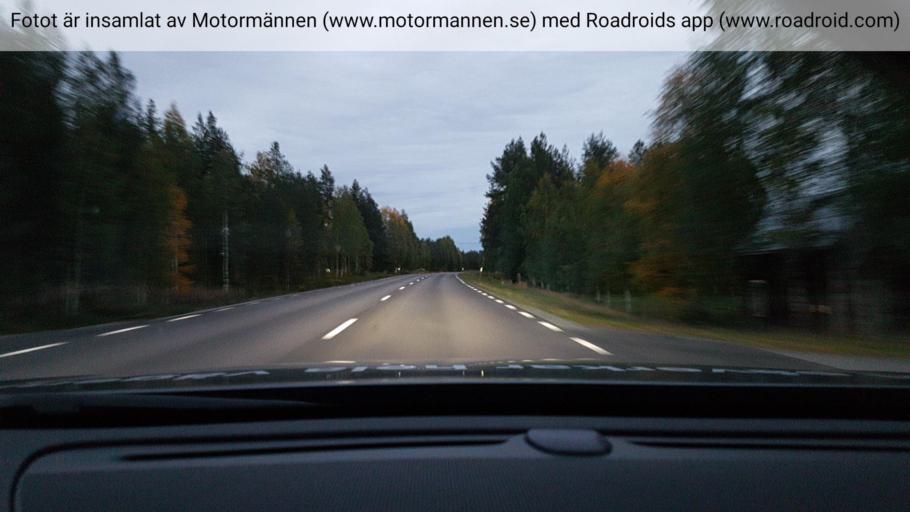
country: SE
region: Norrbotten
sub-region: Alvsbyns Kommun
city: AElvsbyn
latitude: 65.7391
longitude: 20.9656
